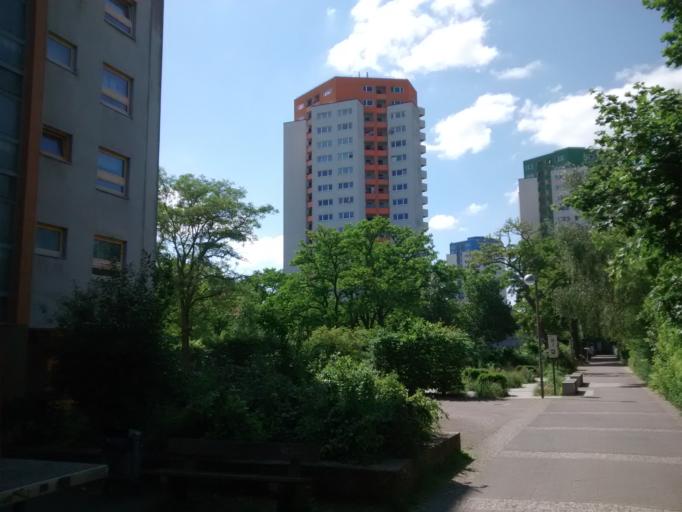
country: DE
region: Berlin
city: Wilhelmstadt
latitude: 52.5217
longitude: 13.1674
